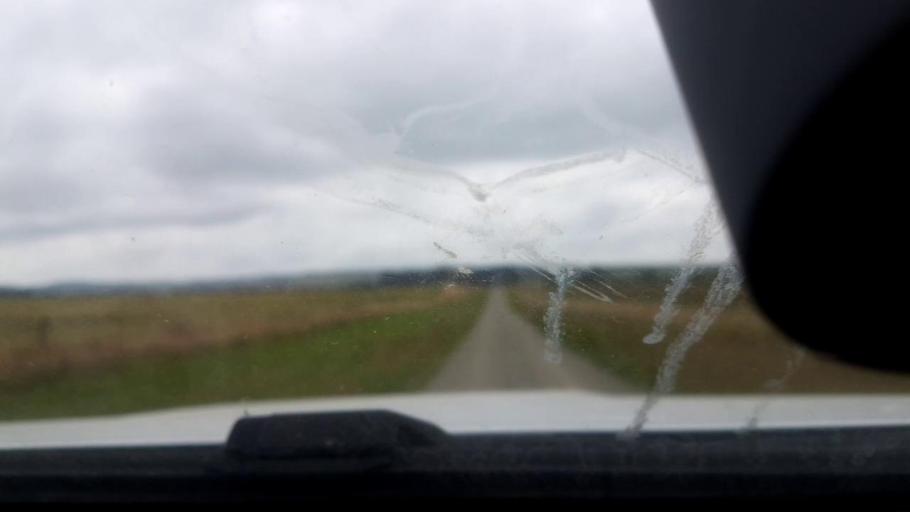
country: NZ
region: Canterbury
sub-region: Timaru District
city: Pleasant Point
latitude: -44.2295
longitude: 171.1659
